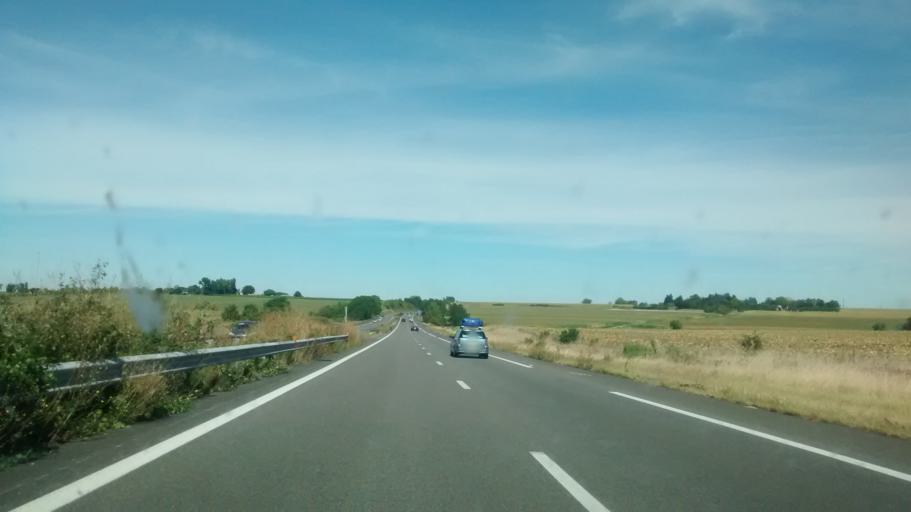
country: FR
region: Poitou-Charentes
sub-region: Departement de la Charente-Maritime
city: Mirambeau
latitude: 45.4157
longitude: -0.6024
